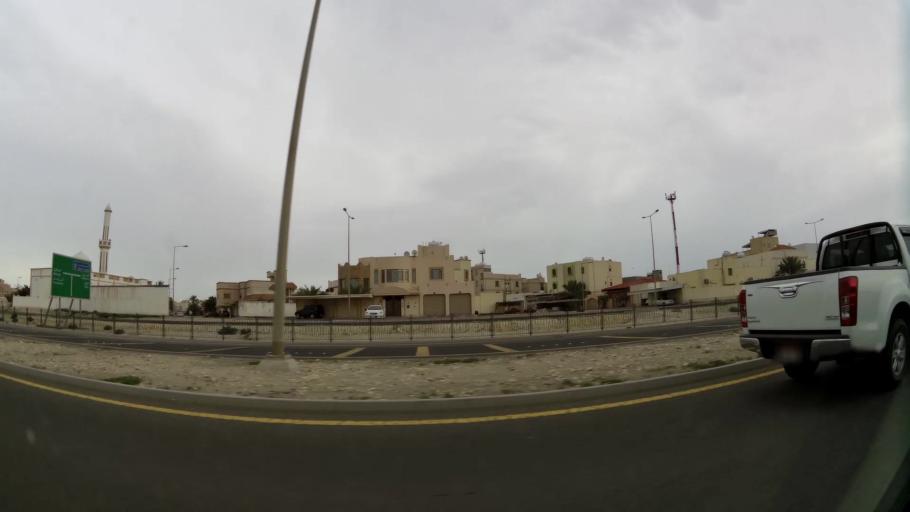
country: BH
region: Central Governorate
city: Madinat Hamad
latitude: 26.1115
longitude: 50.4944
